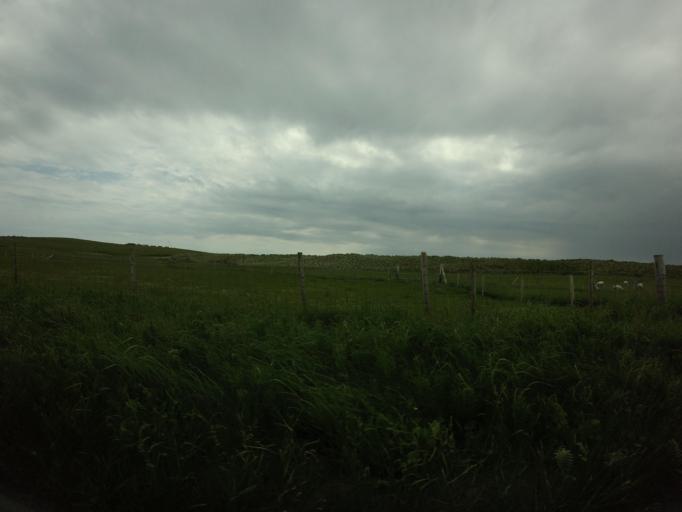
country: GB
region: Scotland
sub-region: Eilean Siar
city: Isle of Lewis
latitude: 58.2701
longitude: -6.3200
